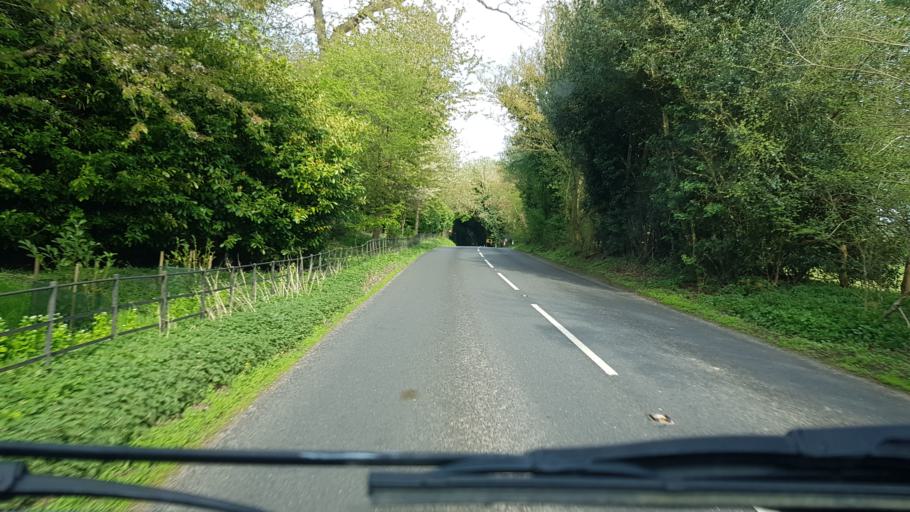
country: GB
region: England
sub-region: Hampshire
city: Overton
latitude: 51.2446
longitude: -1.2208
